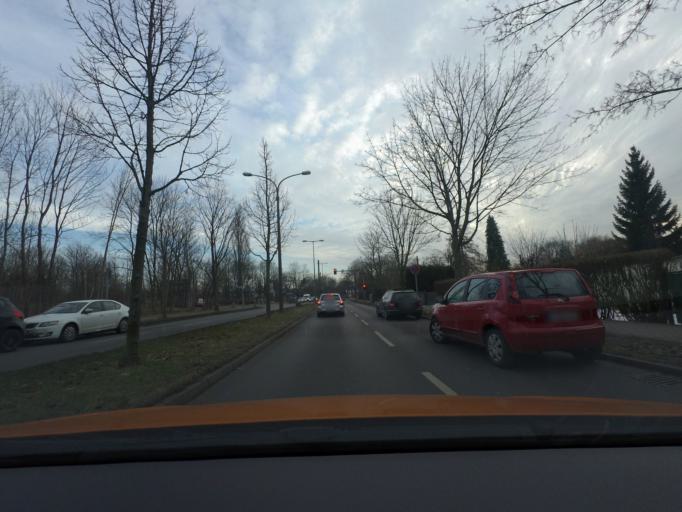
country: DE
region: Berlin
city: Niederschonhausen
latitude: 52.6034
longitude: 13.4017
